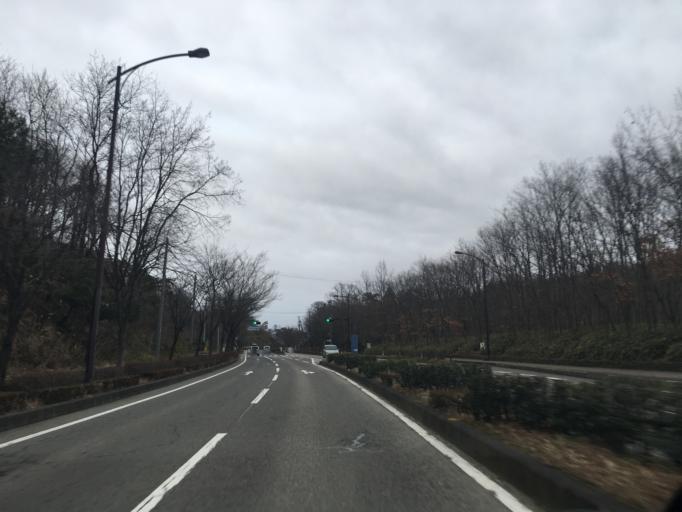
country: JP
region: Fukushima
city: Koriyama
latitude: 37.3936
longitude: 140.4205
